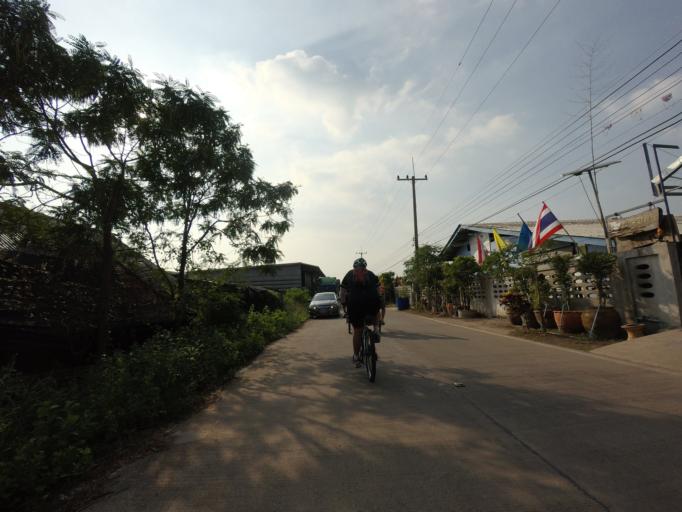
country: TH
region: Samut Sakhon
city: Samut Sakhon
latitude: 13.5080
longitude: 100.3113
